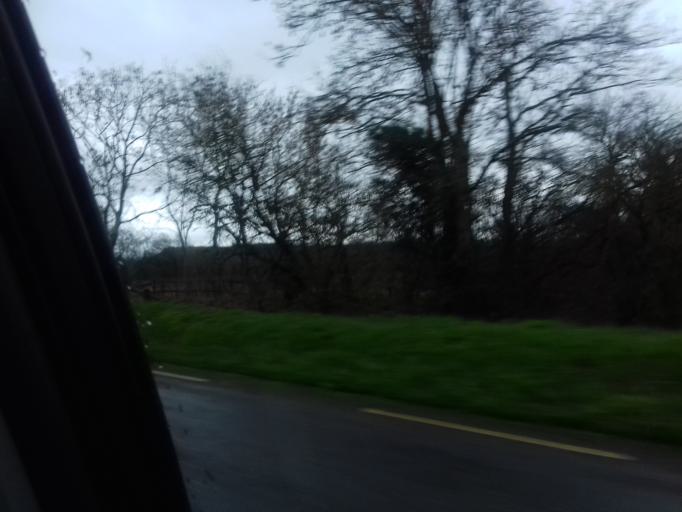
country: IE
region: Leinster
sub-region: County Carlow
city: Bagenalstown
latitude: 52.6369
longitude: -6.9935
